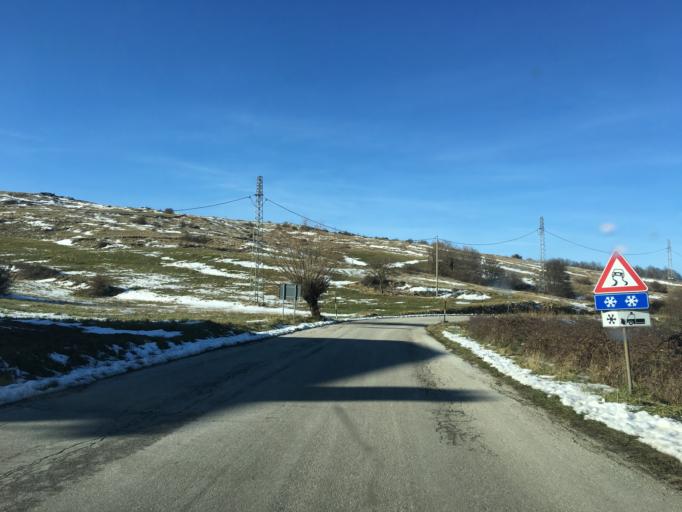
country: IT
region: Abruzzo
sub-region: Provincia di Chieti
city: Rosello
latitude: 41.8566
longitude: 14.3567
